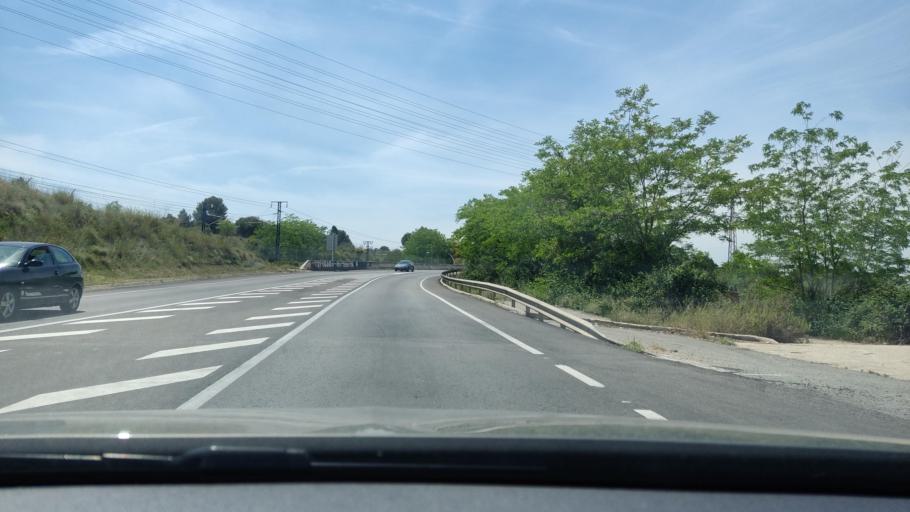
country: ES
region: Catalonia
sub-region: Provincia de Barcelona
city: Sant Sadurni d'Anoia
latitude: 41.4202
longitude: 1.7959
